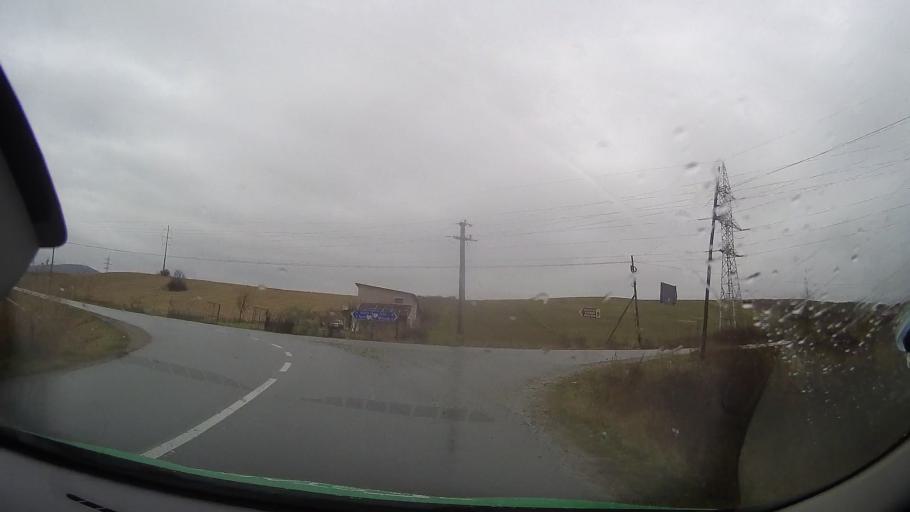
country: RO
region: Bistrita-Nasaud
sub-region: Municipiul Bistrita
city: Viisoara
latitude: 47.0565
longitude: 24.4499
